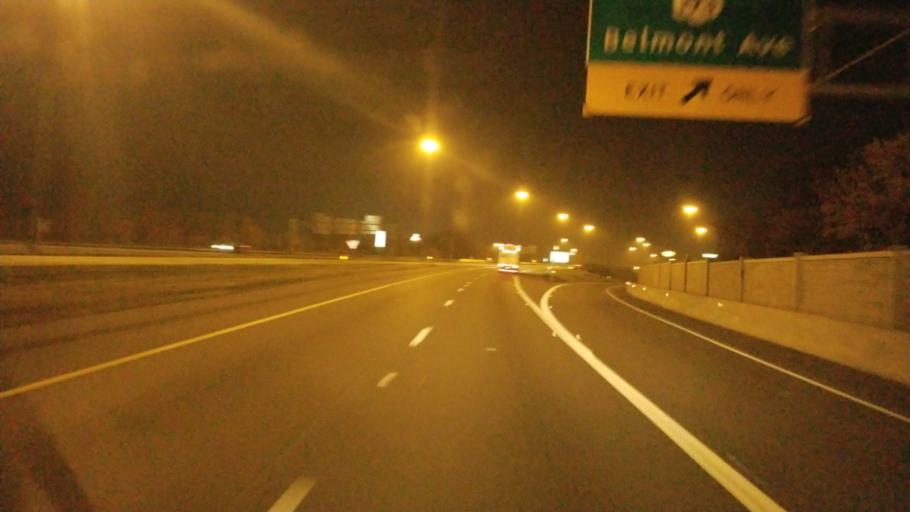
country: US
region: Ohio
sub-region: Trumbull County
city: Churchill
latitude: 41.1504
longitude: -80.6703
